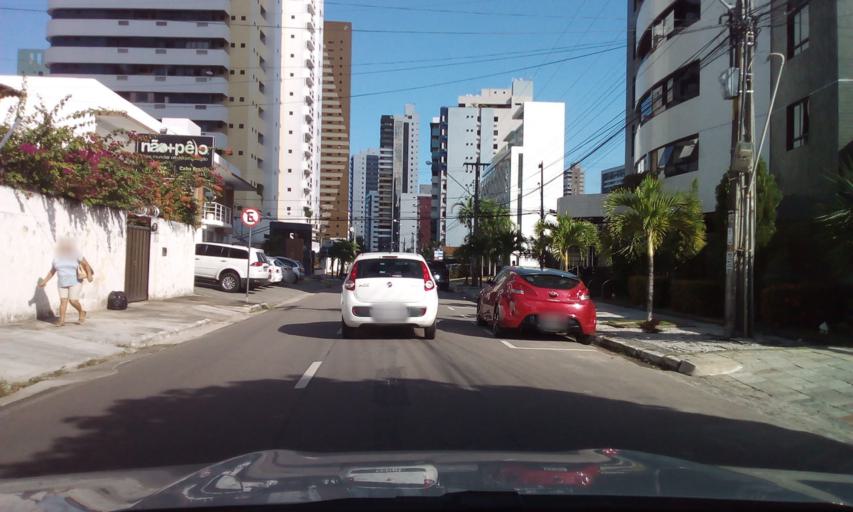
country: BR
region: Paraiba
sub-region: Joao Pessoa
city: Joao Pessoa
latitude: -7.1046
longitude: -34.8354
